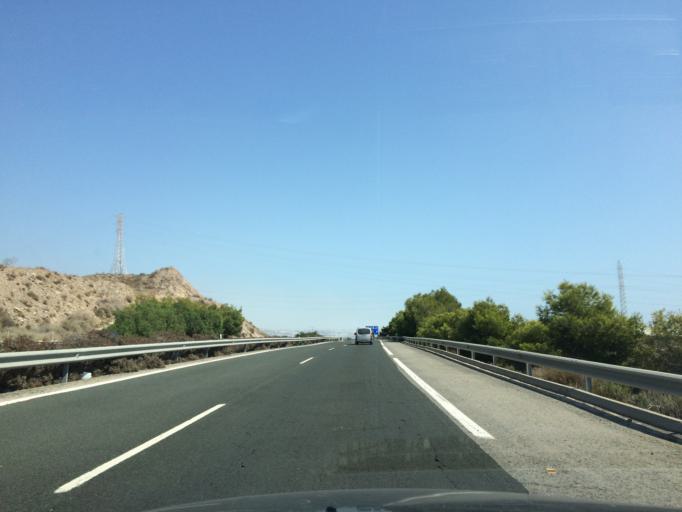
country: ES
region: Andalusia
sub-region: Provincia de Almeria
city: Adra
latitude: 36.7587
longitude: -3.0189
